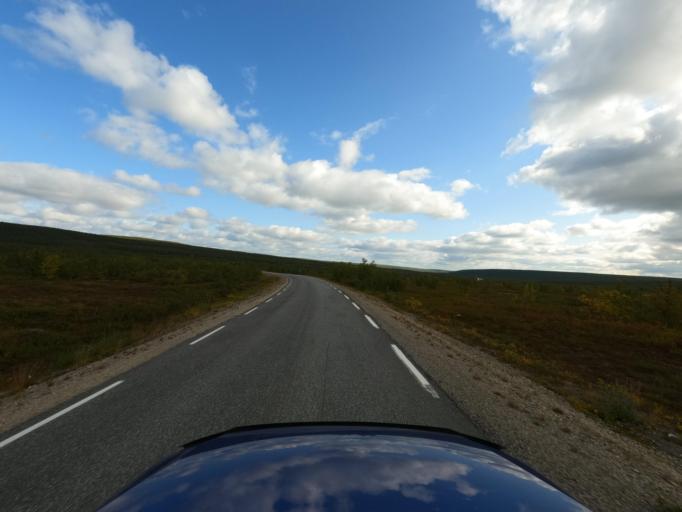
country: NO
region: Finnmark Fylke
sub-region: Porsanger
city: Lakselv
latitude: 69.3707
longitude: 24.3753
